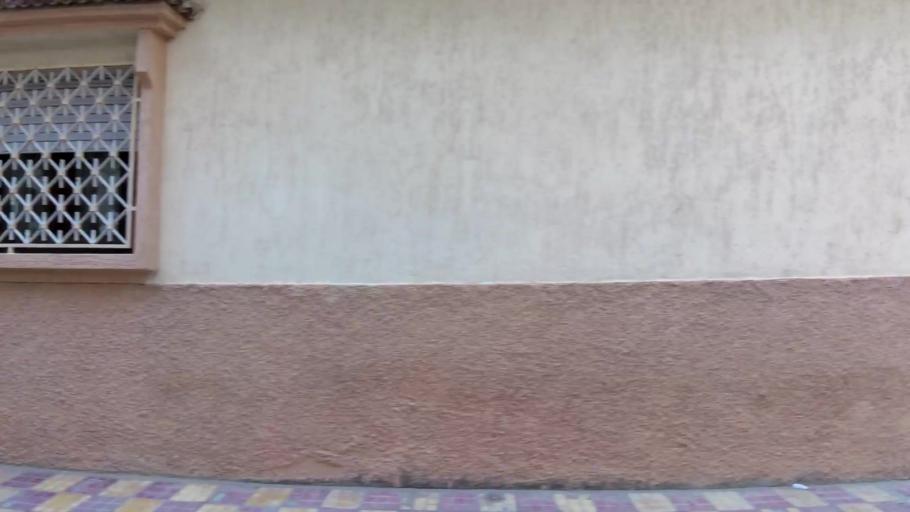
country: MA
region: Tanger-Tetouan
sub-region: Tanger-Assilah
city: Tangier
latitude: 35.7610
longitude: -5.8311
